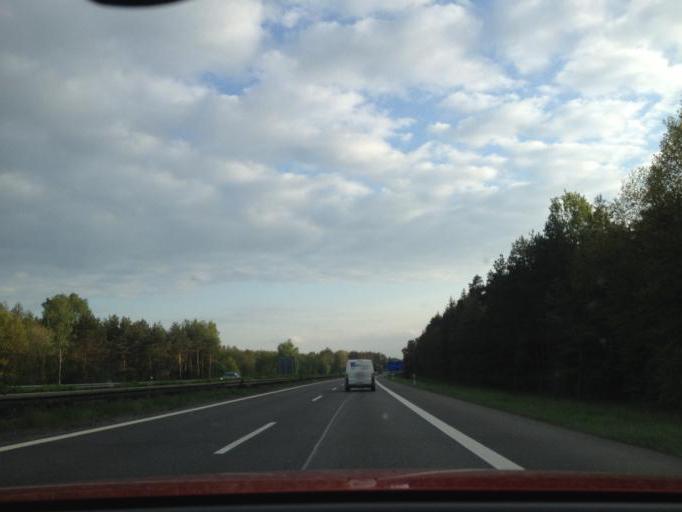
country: DE
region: Bavaria
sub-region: Upper Palatinate
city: Neustadt an der Waldnaab
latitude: 49.7174
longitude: 12.1485
